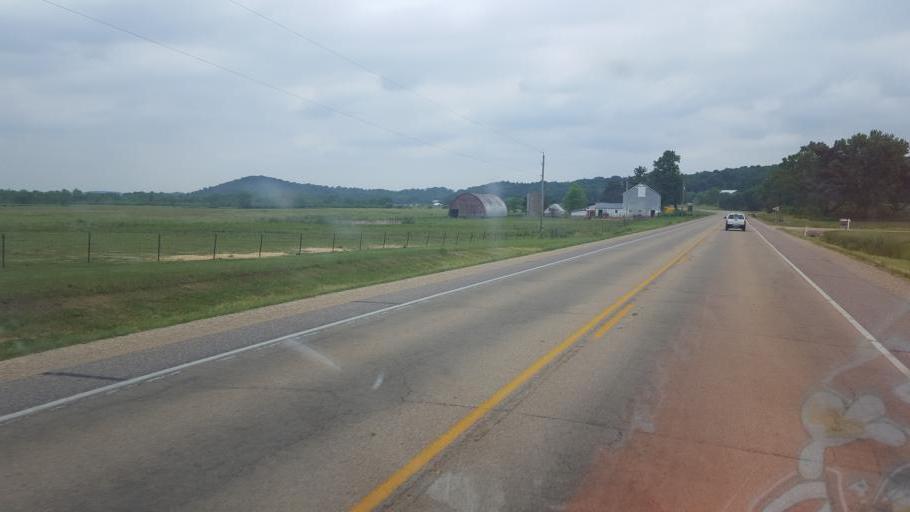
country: US
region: Wisconsin
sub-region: Sauk County
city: Reedsburg
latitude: 43.6091
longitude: -90.1392
